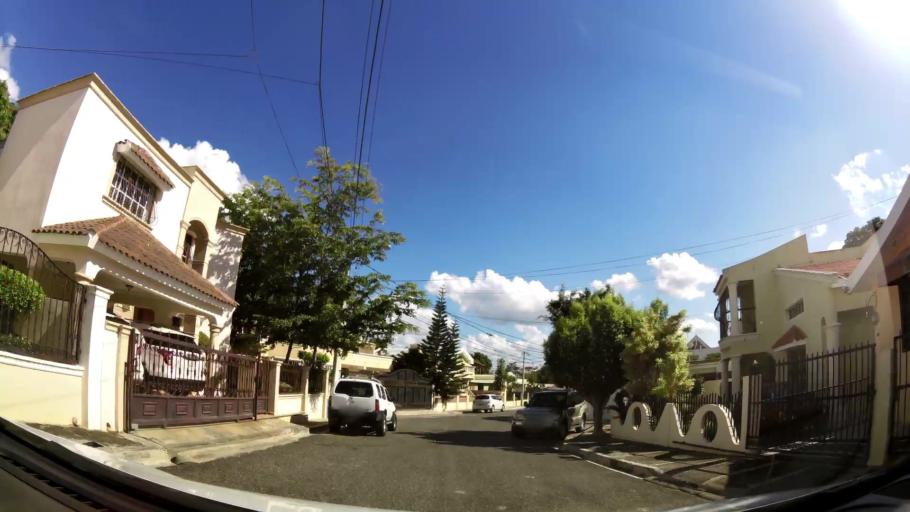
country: DO
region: Santiago
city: Santiago de los Caballeros
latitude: 19.4528
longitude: -70.6675
